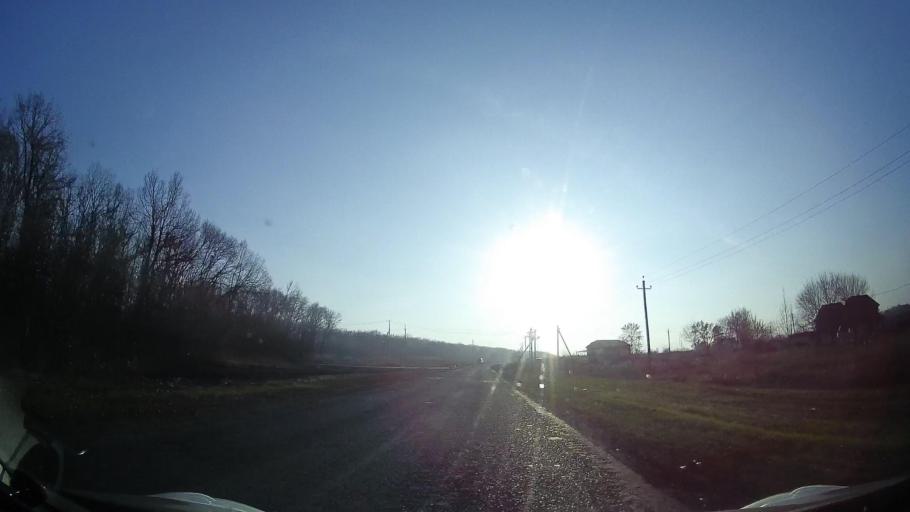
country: RU
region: Rostov
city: Ol'ginskaya
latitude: 47.1382
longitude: 39.8964
